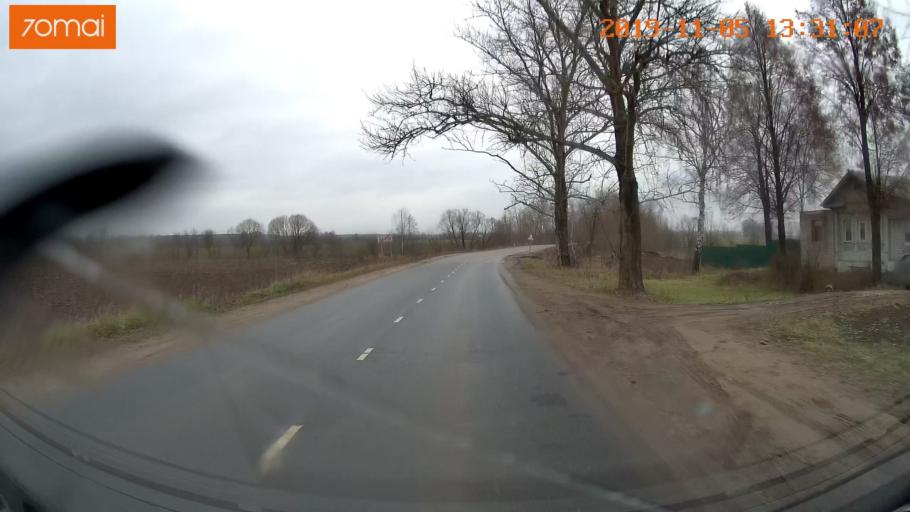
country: RU
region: Ivanovo
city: Shuya
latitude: 56.8723
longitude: 41.3926
